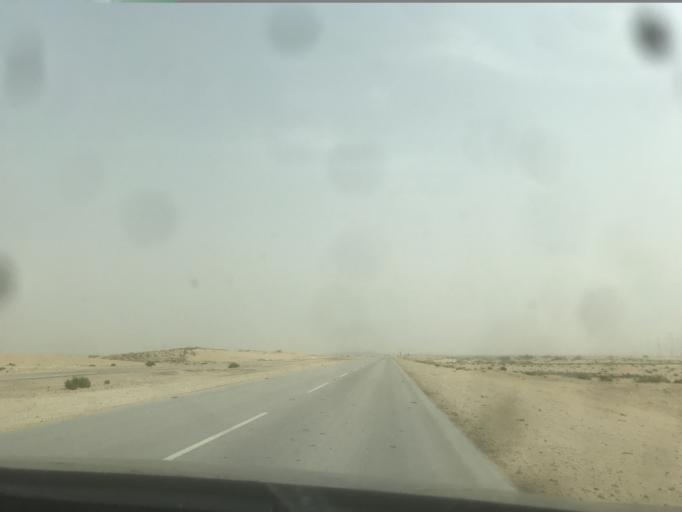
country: SA
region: Eastern Province
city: Abqaiq
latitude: 25.9063
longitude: 49.9179
